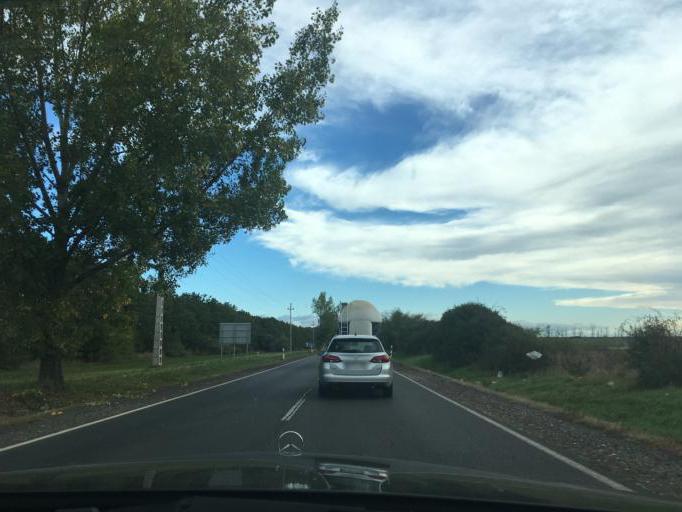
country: HU
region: Borsod-Abauj-Zemplen
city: Arnot
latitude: 48.1218
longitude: 20.8679
